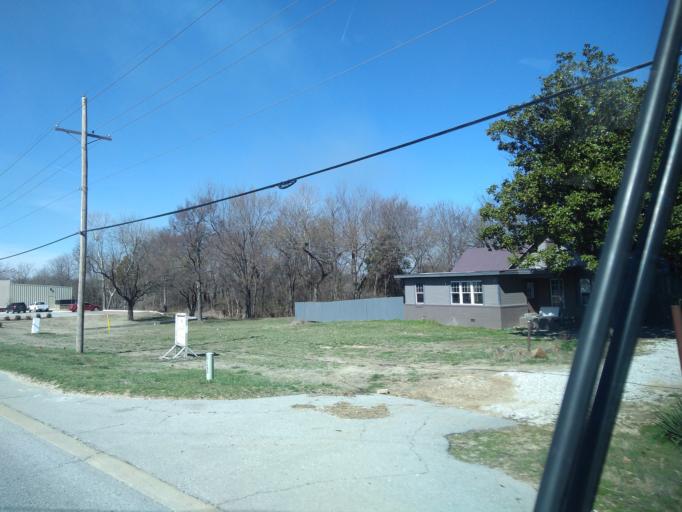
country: US
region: Arkansas
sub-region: Washington County
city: Farmington
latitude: 36.0494
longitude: -94.2137
